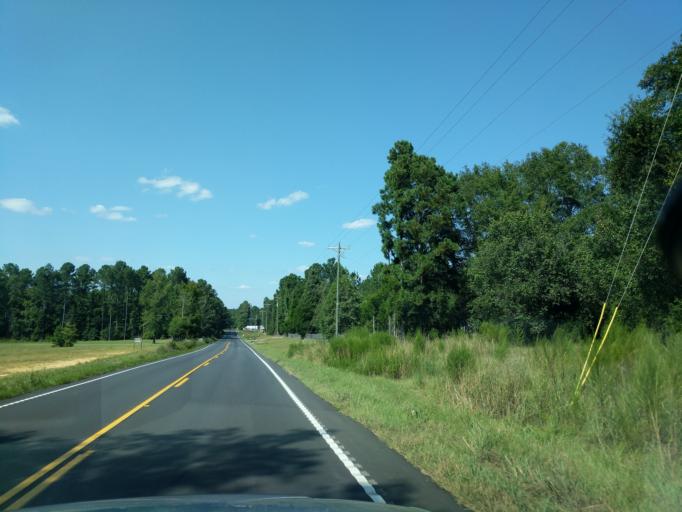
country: US
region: South Carolina
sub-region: Lexington County
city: Batesburg-Leesville
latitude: 33.9432
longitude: -81.5348
